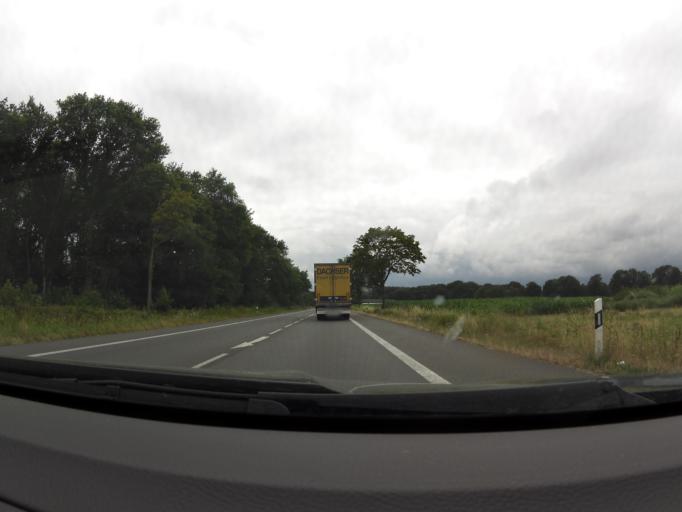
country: DE
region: North Rhine-Westphalia
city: Straelen
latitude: 51.4278
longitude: 6.2709
